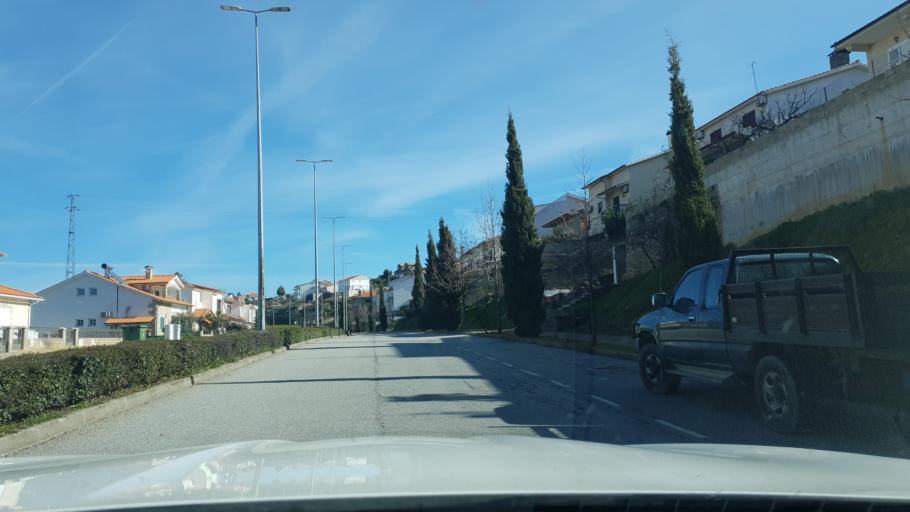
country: PT
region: Braganca
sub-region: Torre de Moncorvo
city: Torre de Moncorvo
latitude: 41.1756
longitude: -7.0447
